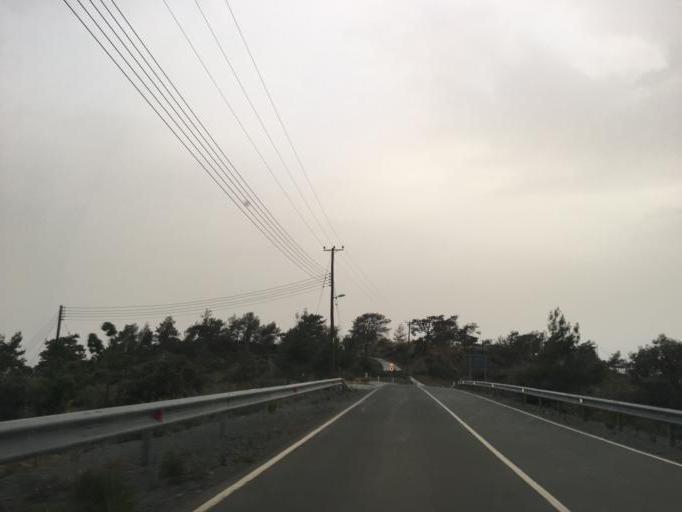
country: CY
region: Limassol
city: Parekklisha
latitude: 34.8082
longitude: 33.1503
